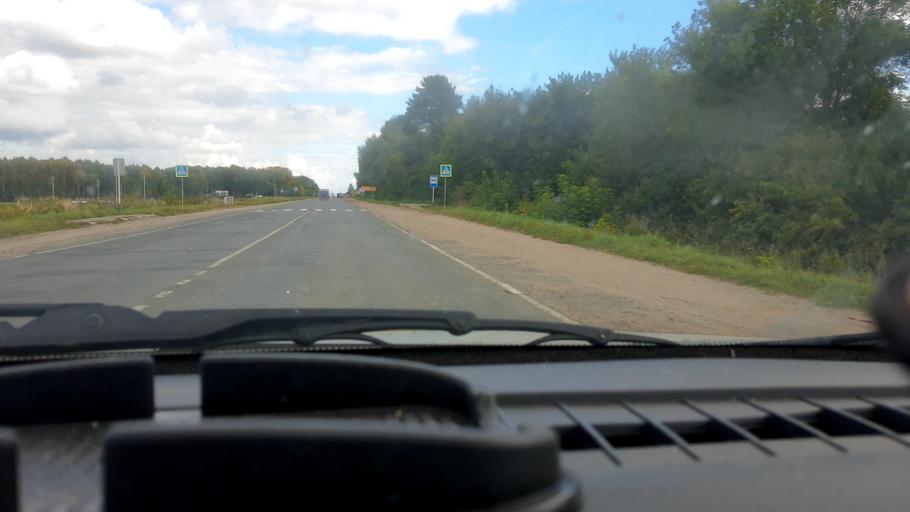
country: RU
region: Mariy-El
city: Medvedevo
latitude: 56.6371
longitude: 47.7534
